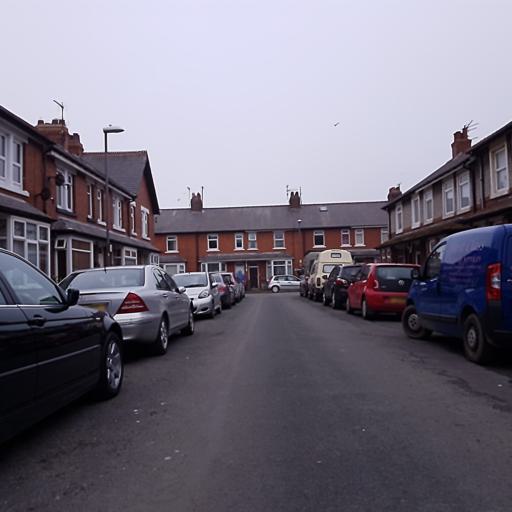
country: GB
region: England
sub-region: North Yorkshire
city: Filey
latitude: 54.2106
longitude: -0.2908
